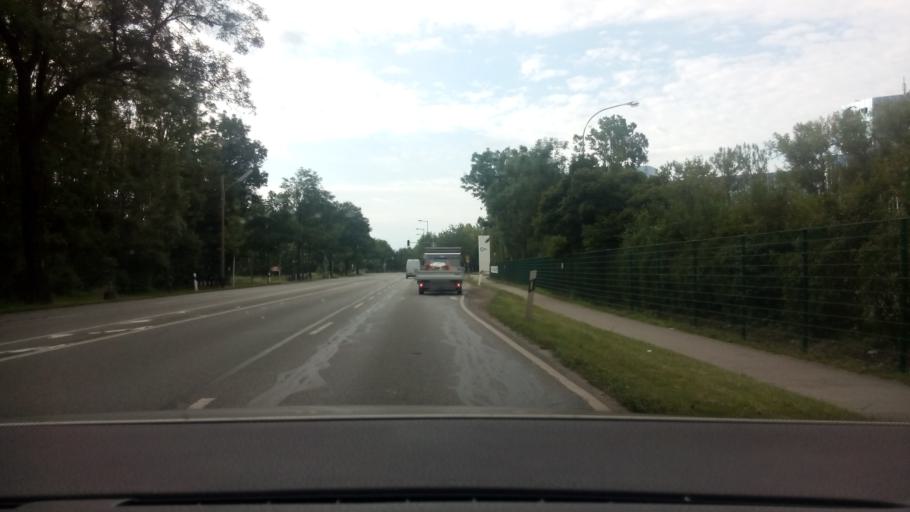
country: DE
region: Bavaria
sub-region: Upper Bavaria
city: Karlsfeld
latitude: 48.2148
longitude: 11.4823
